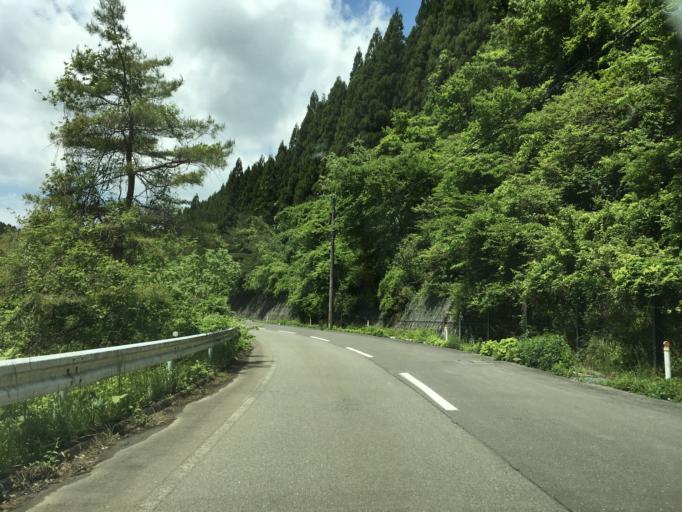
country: JP
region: Miyagi
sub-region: Oshika Gun
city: Onagawa Cho
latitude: 38.6732
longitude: 141.3581
